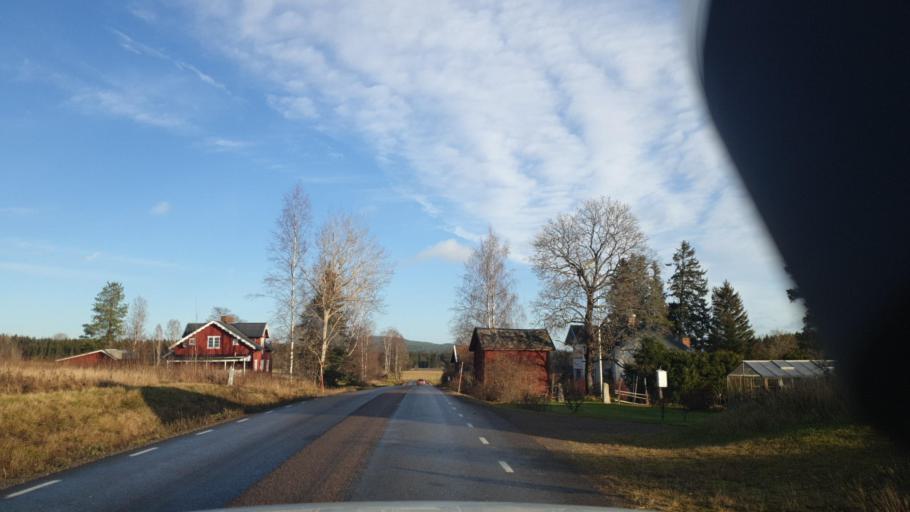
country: SE
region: Vaermland
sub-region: Eda Kommun
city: Charlottenberg
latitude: 59.7801
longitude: 12.1730
